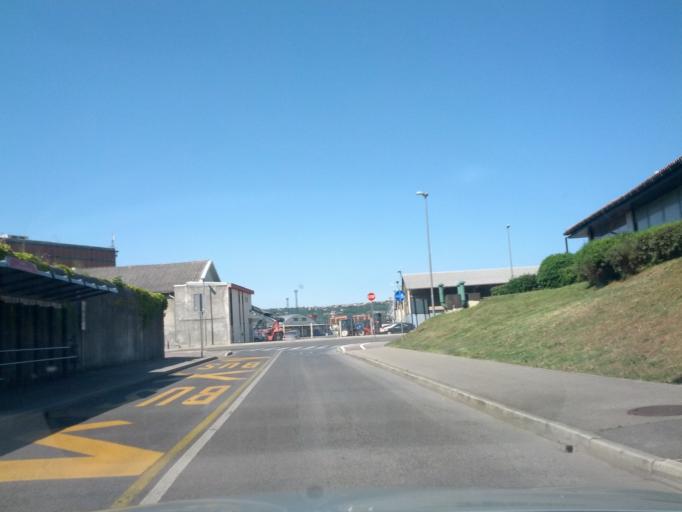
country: SI
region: Koper-Capodistria
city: Koper
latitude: 45.5484
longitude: 13.7367
